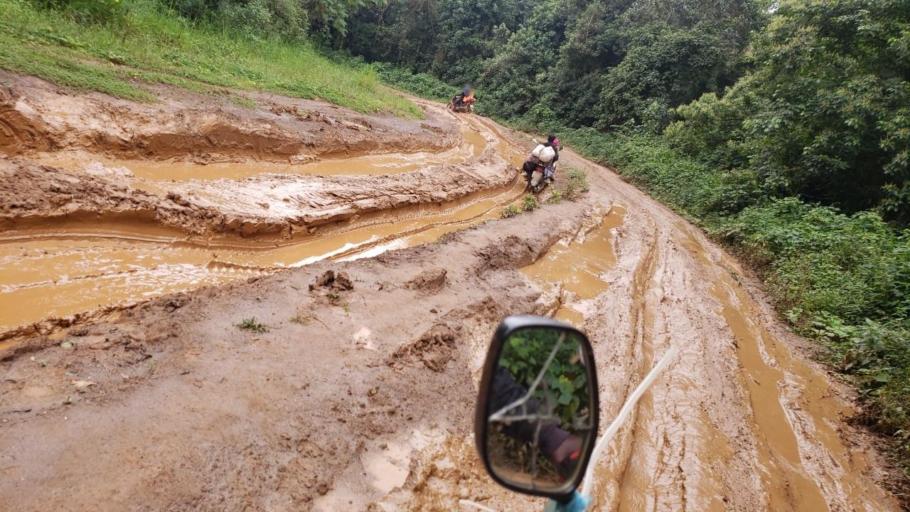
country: CD
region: South Kivu
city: Kabare
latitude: -2.2531
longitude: 28.6470
